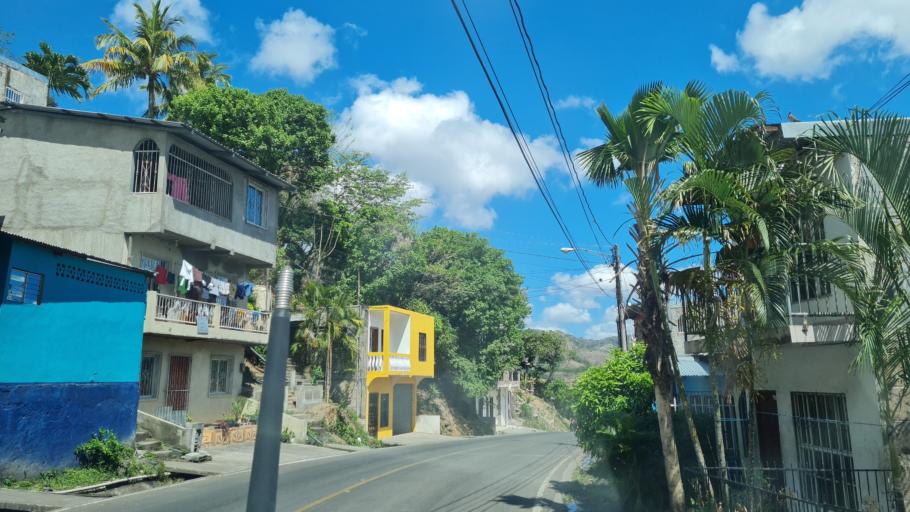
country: NI
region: Boaco
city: Boaco
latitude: 12.4672
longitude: -85.6564
